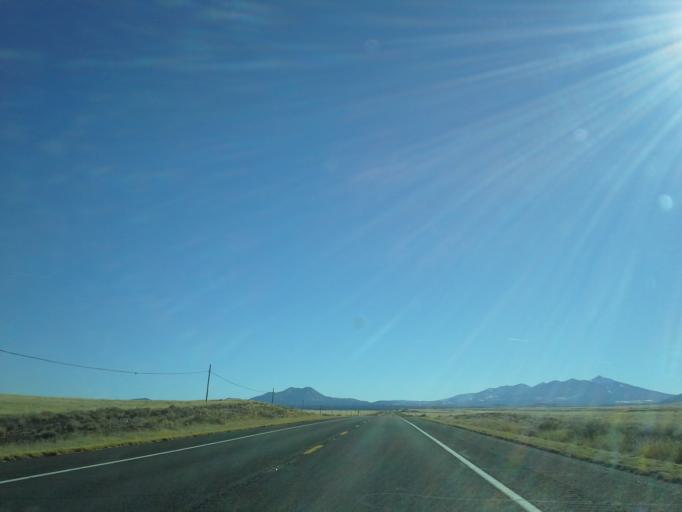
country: US
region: Arizona
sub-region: Coconino County
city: Flagstaff
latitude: 35.6109
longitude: -111.5239
